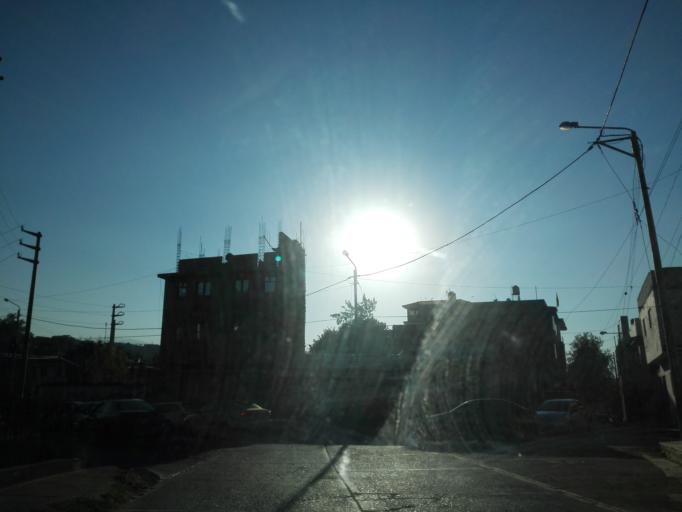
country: PE
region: Ayacucho
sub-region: Provincia de Huamanga
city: Ayacucho
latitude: -13.1634
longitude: -74.2226
